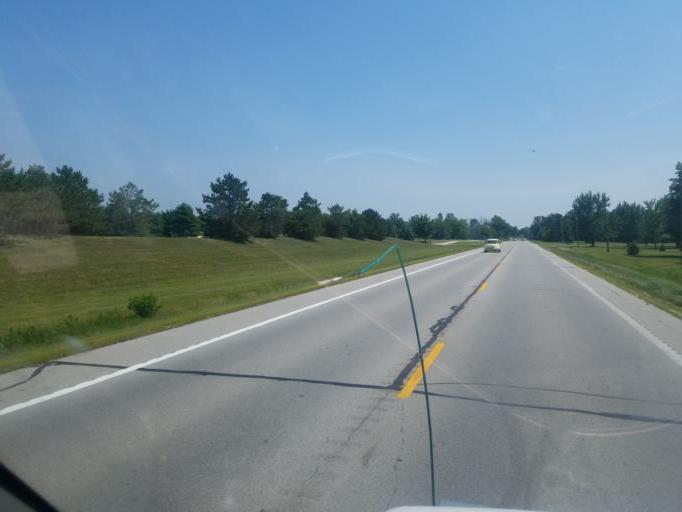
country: US
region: Ohio
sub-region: Mercer County
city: Celina
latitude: 40.5150
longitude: -84.5775
